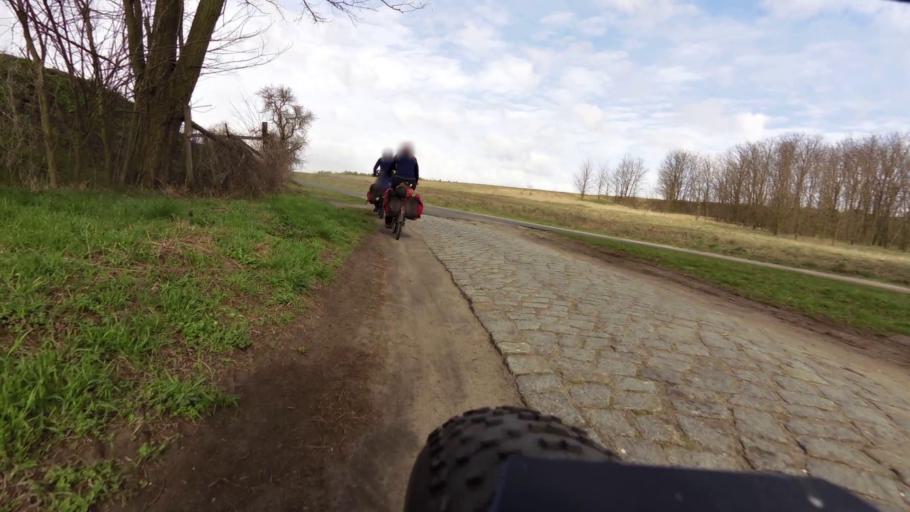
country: DE
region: Brandenburg
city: Brieskow-Finkenheerd
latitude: 52.2855
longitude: 14.6179
